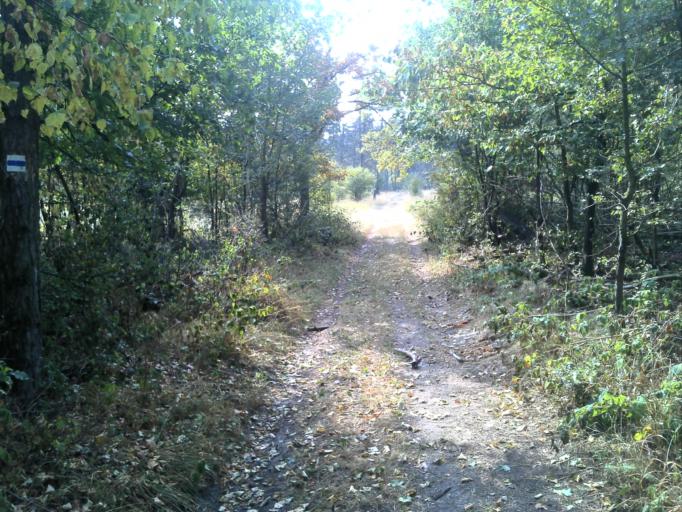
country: HU
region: Komarom-Esztergom
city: Oroszlany
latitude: 47.4109
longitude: 18.3605
